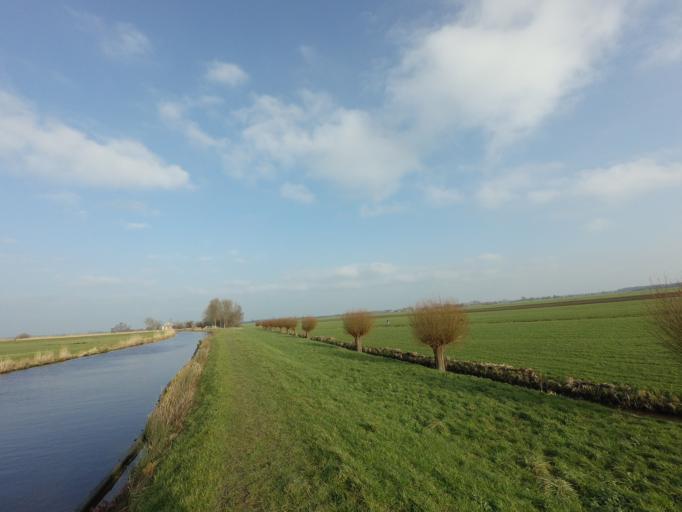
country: NL
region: Utrecht
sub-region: Gemeente Woerden
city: Woerden
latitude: 52.1010
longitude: 4.8686
